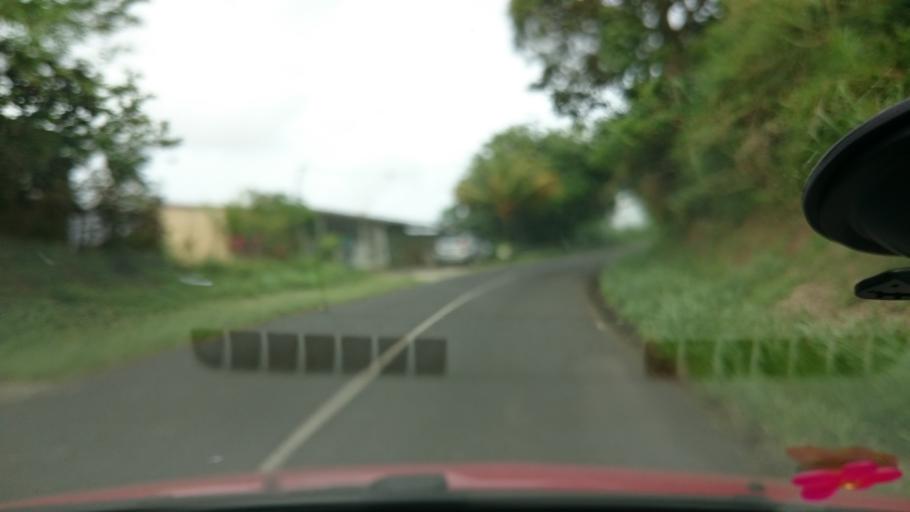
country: MQ
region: Martinique
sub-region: Martinique
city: Riviere-Pilote
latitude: 14.4949
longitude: -60.9246
